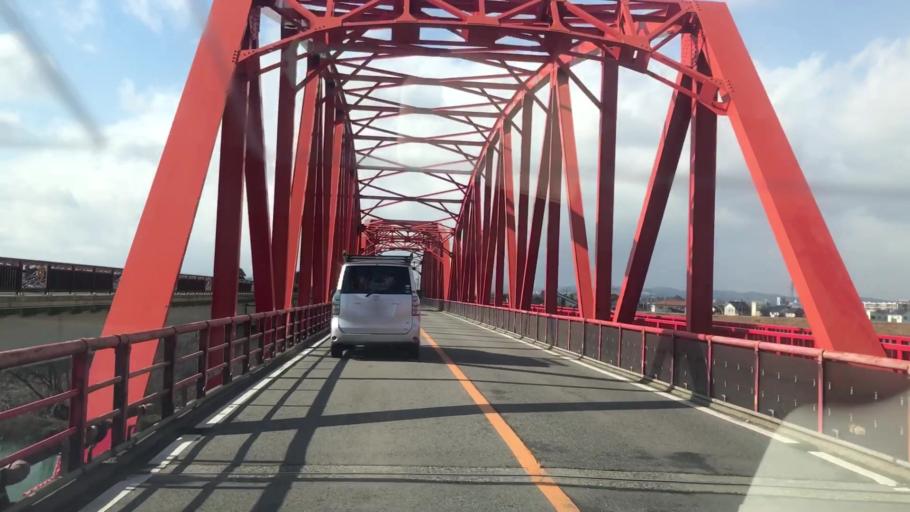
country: JP
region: Toyama
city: Takaoka
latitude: 36.7352
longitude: 137.0433
